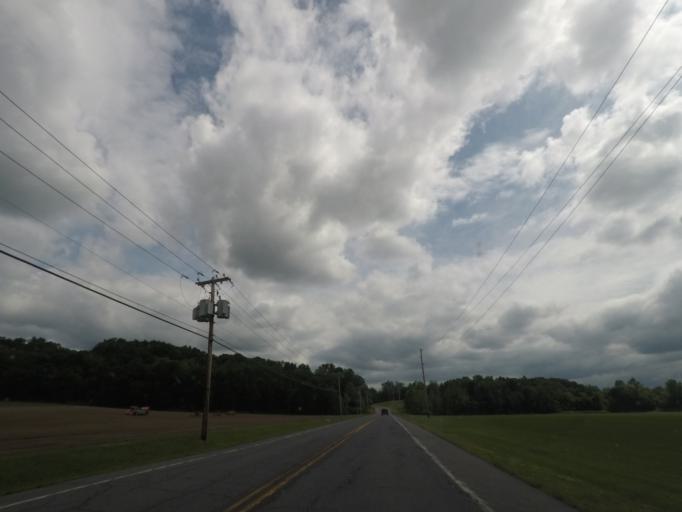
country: US
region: New York
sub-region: Saratoga County
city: Stillwater
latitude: 42.9206
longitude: -73.6310
